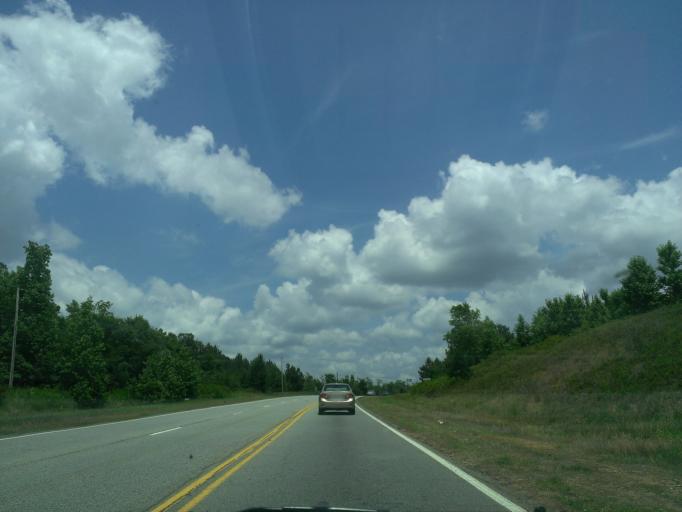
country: US
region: Georgia
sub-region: Oconee County
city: Watkinsville
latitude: 33.9084
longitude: -83.4649
